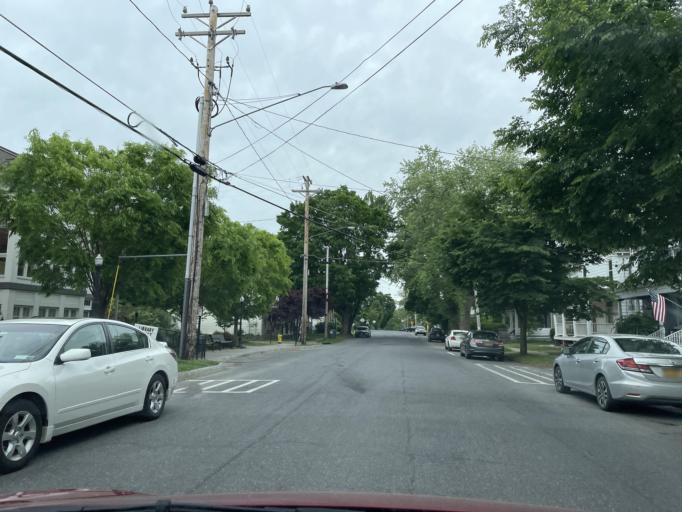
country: US
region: New York
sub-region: Ulster County
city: Saugerties
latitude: 42.0778
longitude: -73.9496
